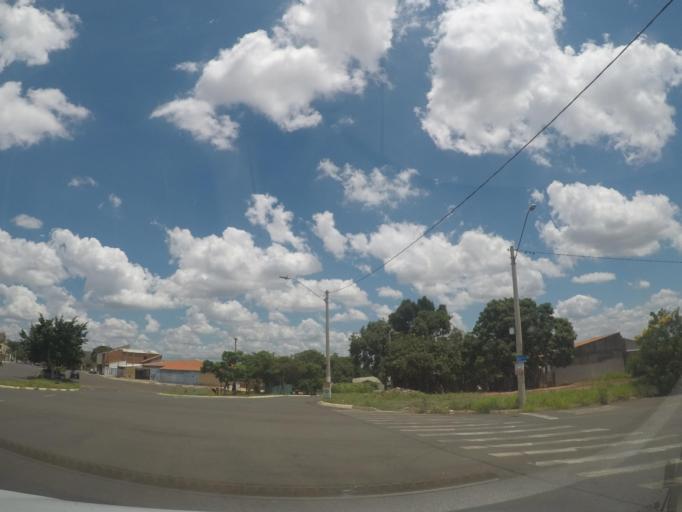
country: BR
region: Sao Paulo
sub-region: Hortolandia
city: Hortolandia
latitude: -22.8396
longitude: -47.2251
